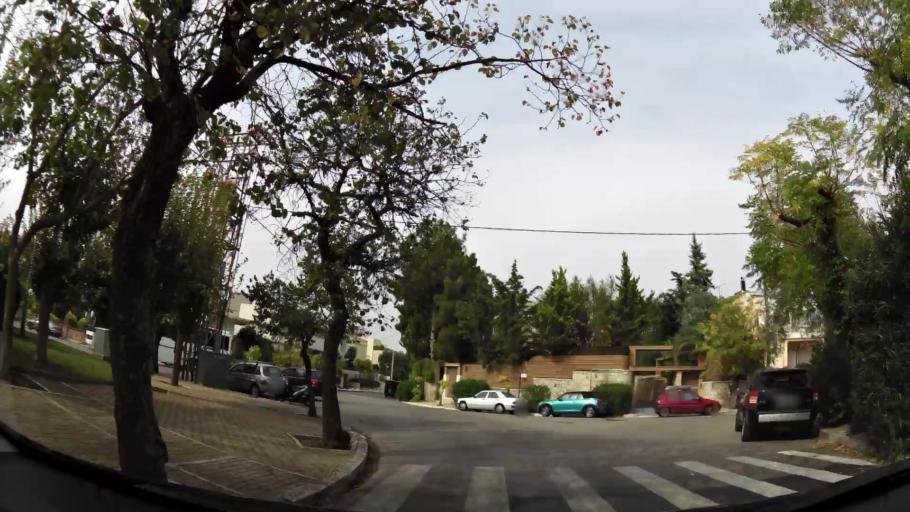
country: GR
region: Attica
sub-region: Nomarchia Athinas
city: Filothei
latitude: 38.0223
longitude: 23.7832
